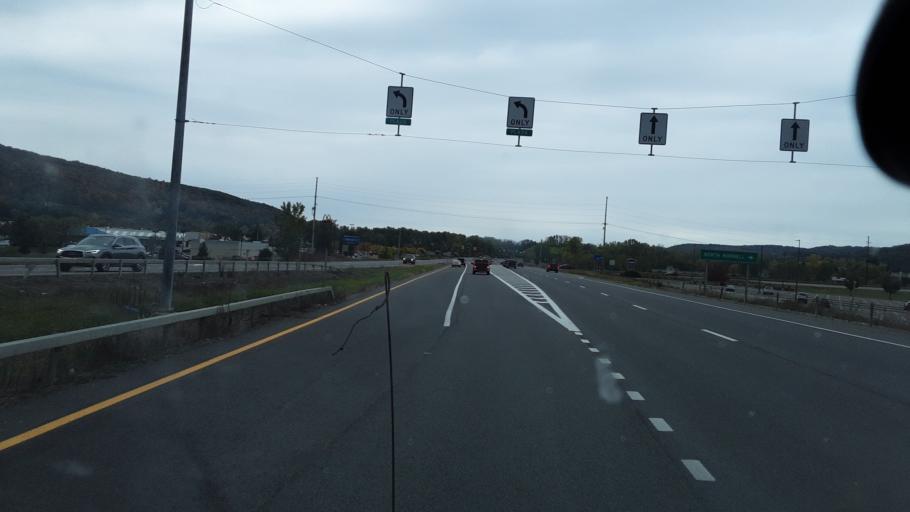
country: US
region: New York
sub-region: Steuben County
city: Hornell
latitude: 42.3437
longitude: -77.6649
